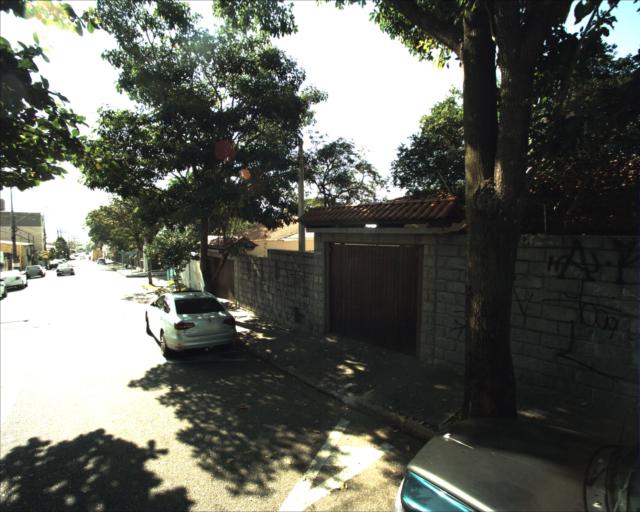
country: BR
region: Sao Paulo
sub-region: Sorocaba
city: Sorocaba
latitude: -23.4847
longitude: -47.4501
